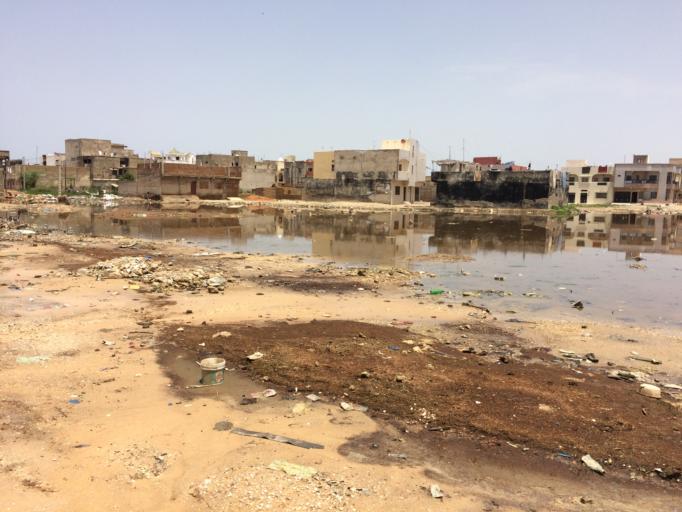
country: SN
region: Dakar
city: Pikine
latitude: 14.7368
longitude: -17.3301
